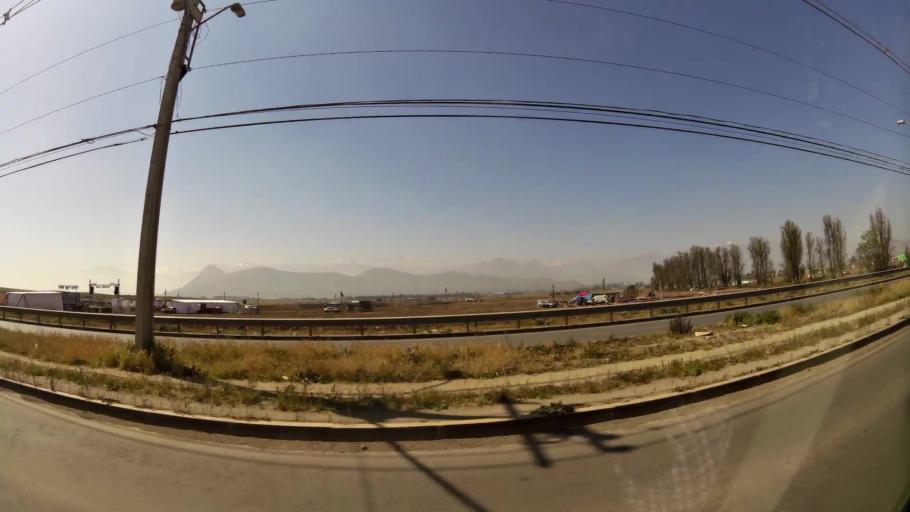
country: CL
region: Santiago Metropolitan
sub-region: Provincia de Santiago
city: Lo Prado
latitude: -33.3454
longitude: -70.7410
